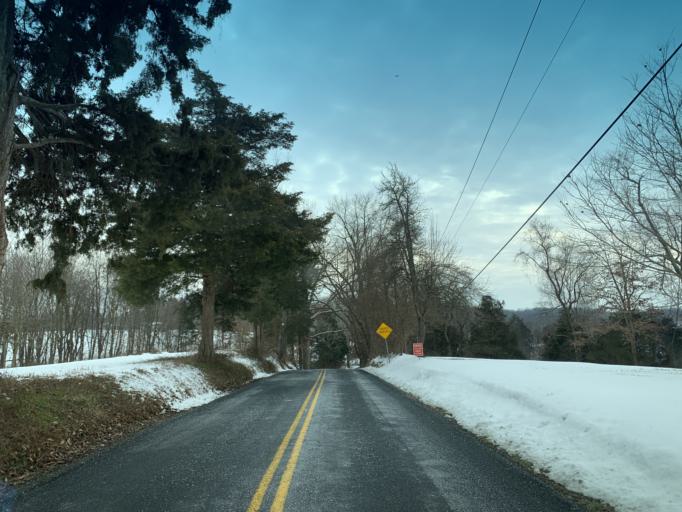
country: US
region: Pennsylvania
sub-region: York County
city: Susquehanna Trails
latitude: 39.7103
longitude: -76.2996
